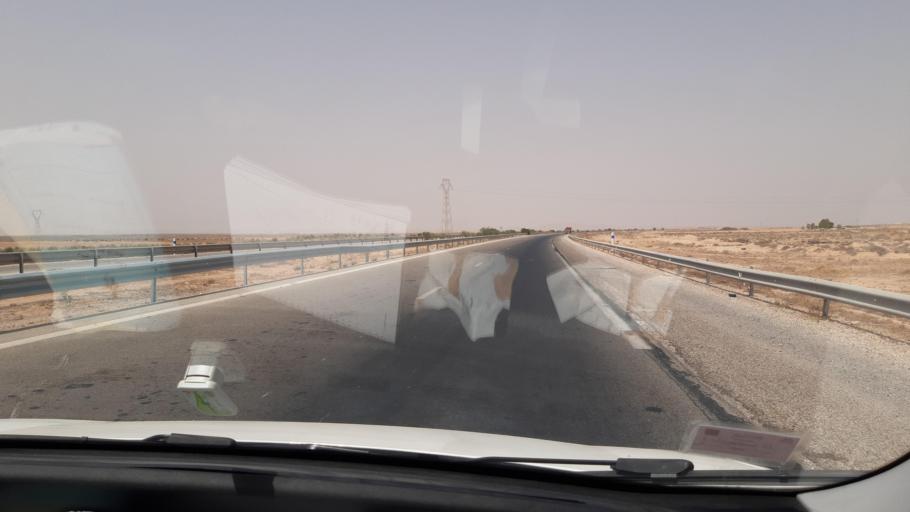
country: TN
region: Qabis
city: Gabes
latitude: 33.9127
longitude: 9.9705
